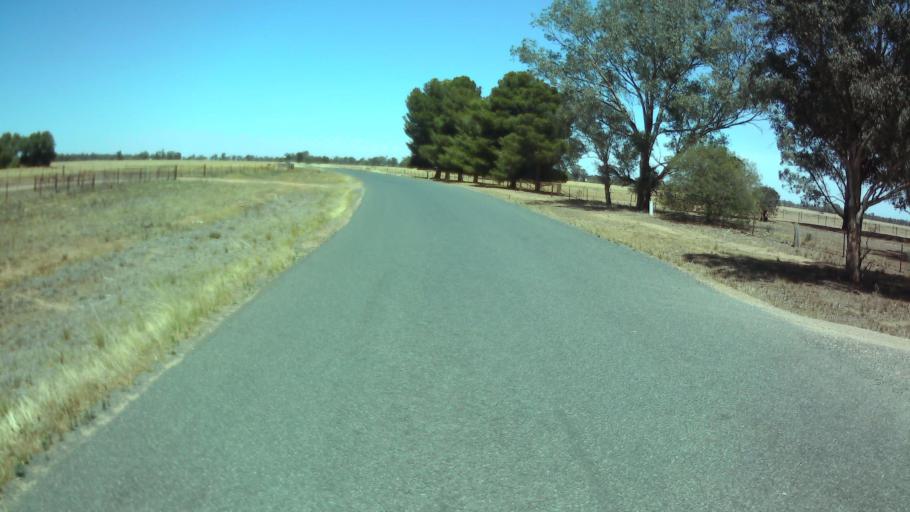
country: AU
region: New South Wales
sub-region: Weddin
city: Grenfell
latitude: -34.0469
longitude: 147.7826
